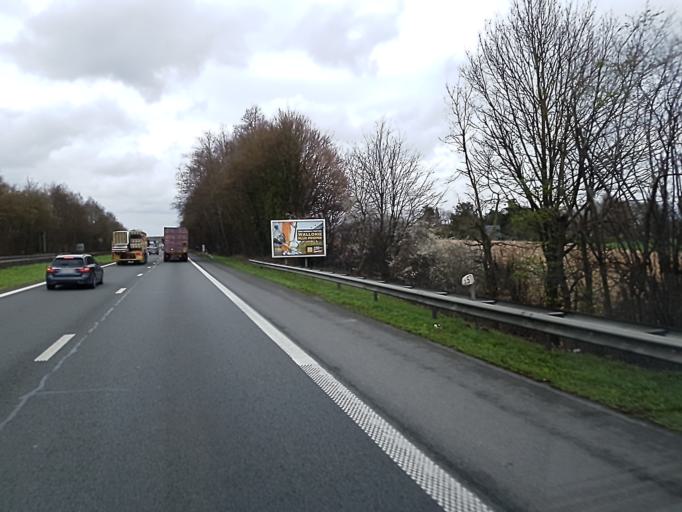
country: FR
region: Nord-Pas-de-Calais
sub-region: Departement du Nord
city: Camphin-en-Pevele
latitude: 50.6298
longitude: 3.3114
